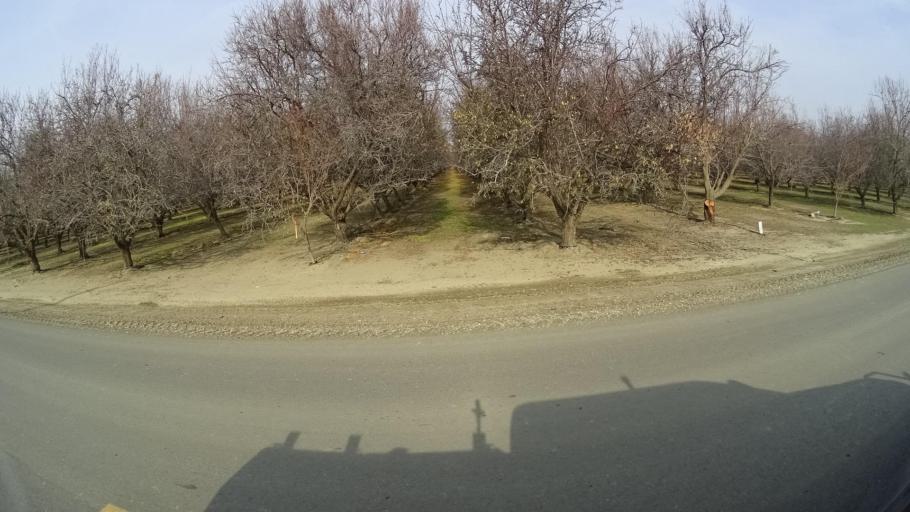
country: US
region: California
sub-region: Kern County
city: Arvin
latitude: 35.0455
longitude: -118.8930
